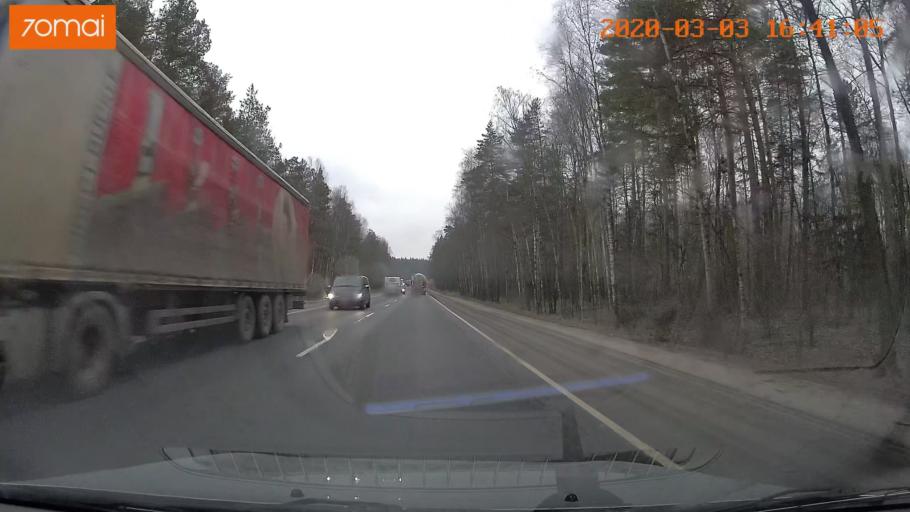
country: RU
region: Moskovskaya
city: Lopatinskiy
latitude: 55.3626
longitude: 38.7353
